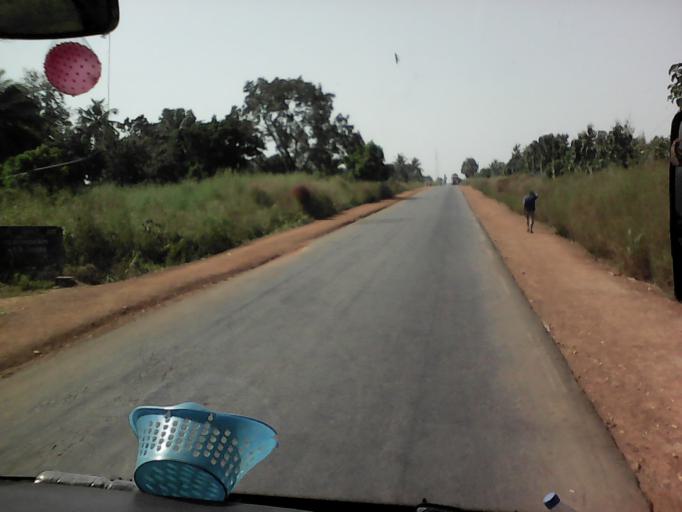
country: TG
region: Centrale
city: Sotouboua
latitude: 8.7386
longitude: 1.0519
